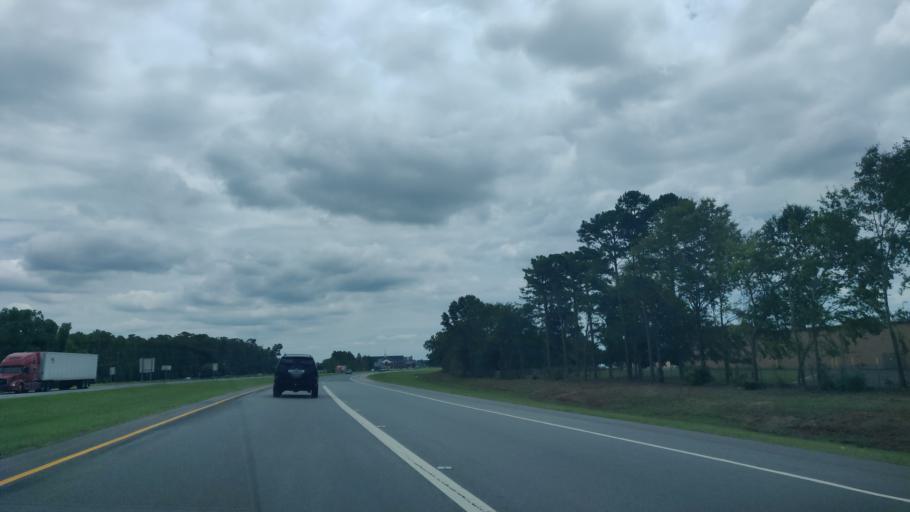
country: US
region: Georgia
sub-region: Dougherty County
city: Albany
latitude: 31.6228
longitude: -84.2258
